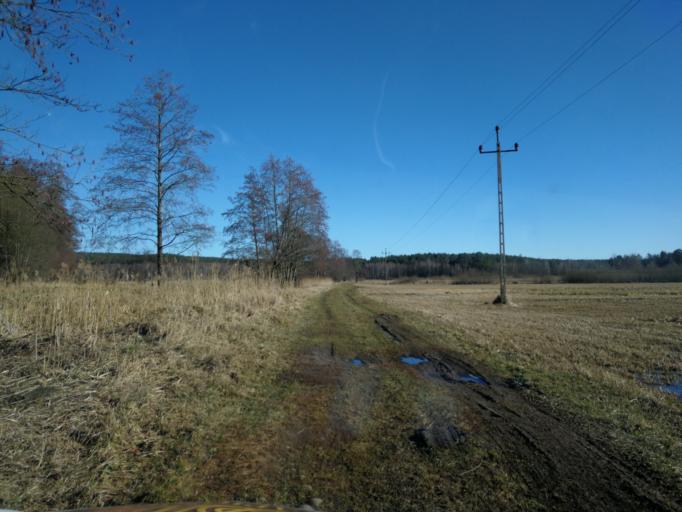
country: PL
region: Kujawsko-Pomorskie
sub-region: Powiat brodnicki
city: Gorzno
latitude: 53.2349
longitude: 19.6687
